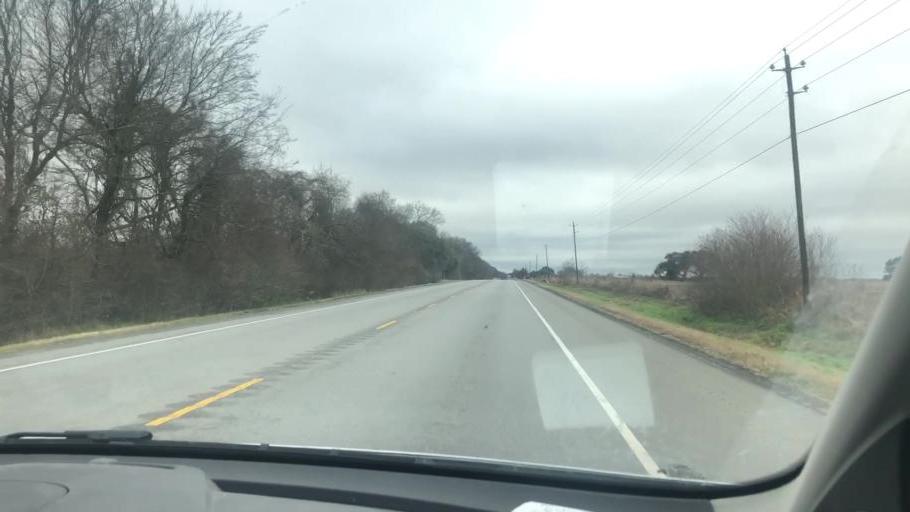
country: US
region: Texas
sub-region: Matagorda County
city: Bay City
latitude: 29.0765
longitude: -95.9727
